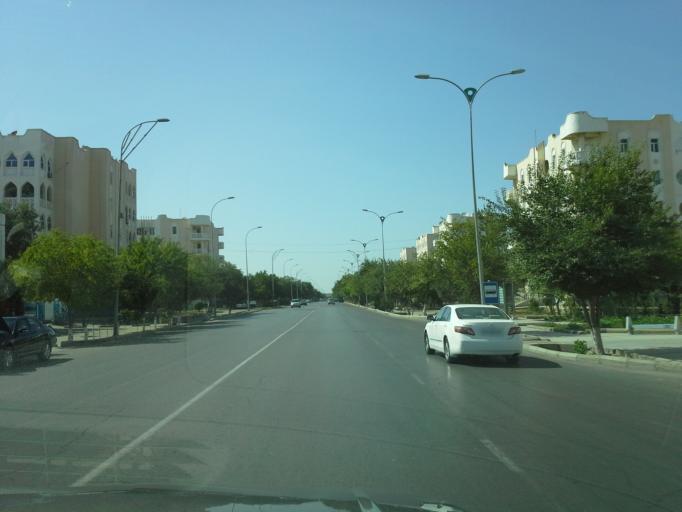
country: TM
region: Dasoguz
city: Dasoguz
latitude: 41.8366
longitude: 59.9576
